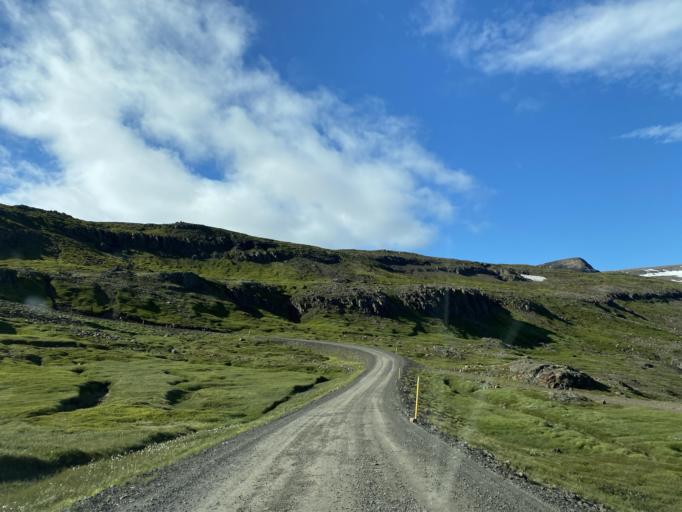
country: IS
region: East
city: Eskifjoerdur
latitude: 65.1798
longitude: -14.0888
